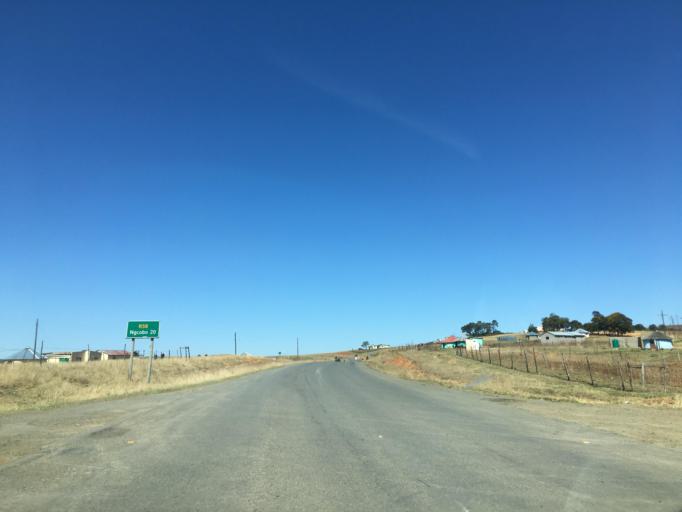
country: ZA
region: Eastern Cape
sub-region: Chris Hani District Municipality
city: Cala
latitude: -31.5572
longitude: 27.8968
